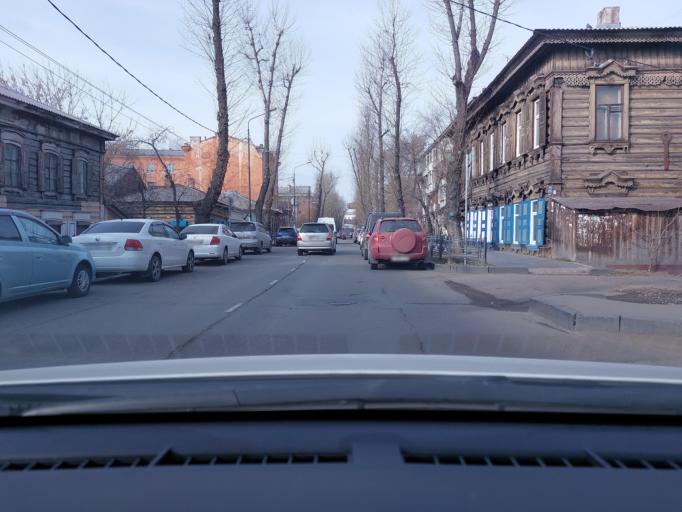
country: RU
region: Irkutsk
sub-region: Irkutskiy Rayon
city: Irkutsk
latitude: 52.2814
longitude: 104.2902
